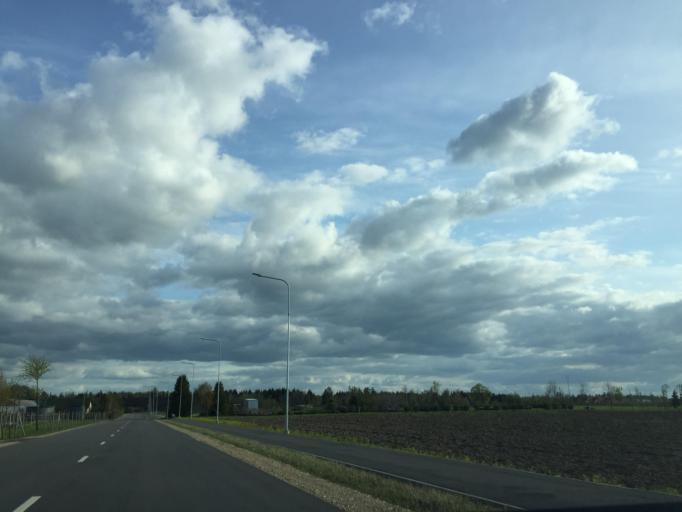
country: LV
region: Sigulda
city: Sigulda
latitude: 57.1353
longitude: 24.8618
